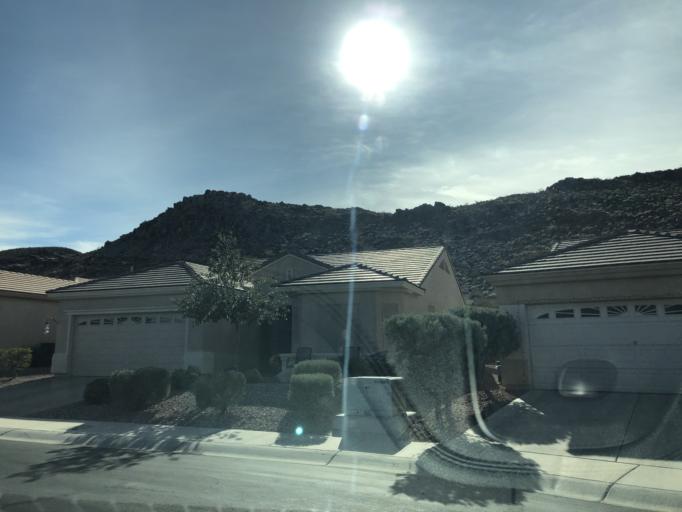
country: US
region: Nevada
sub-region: Clark County
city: Whitney
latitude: 36.0017
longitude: -115.0798
